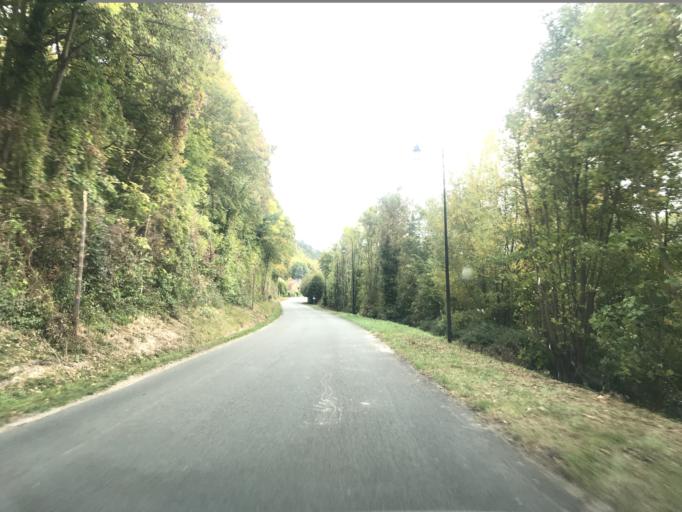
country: FR
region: Haute-Normandie
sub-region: Departement de l'Eure
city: Acquigny
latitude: 49.1772
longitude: 1.1850
